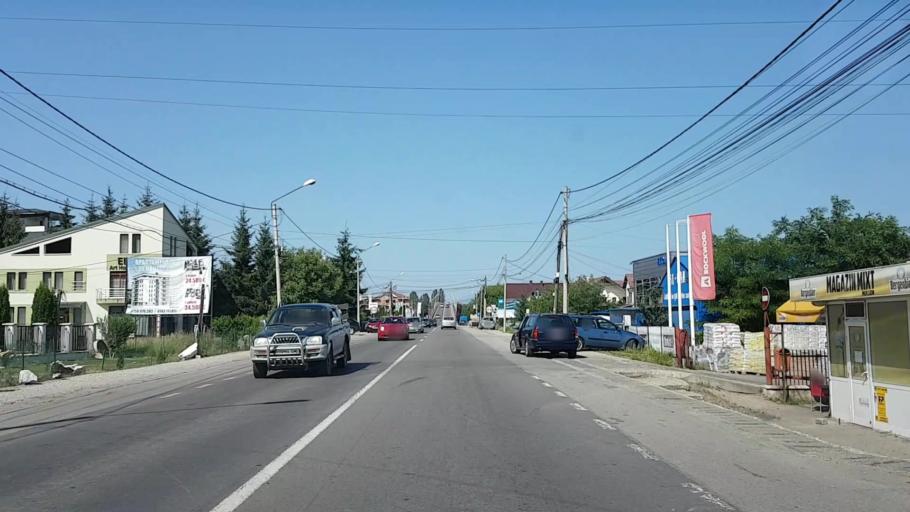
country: RO
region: Bistrita-Nasaud
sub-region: Municipiul Bistrita
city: Viisoara
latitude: 47.1131
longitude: 24.4616
